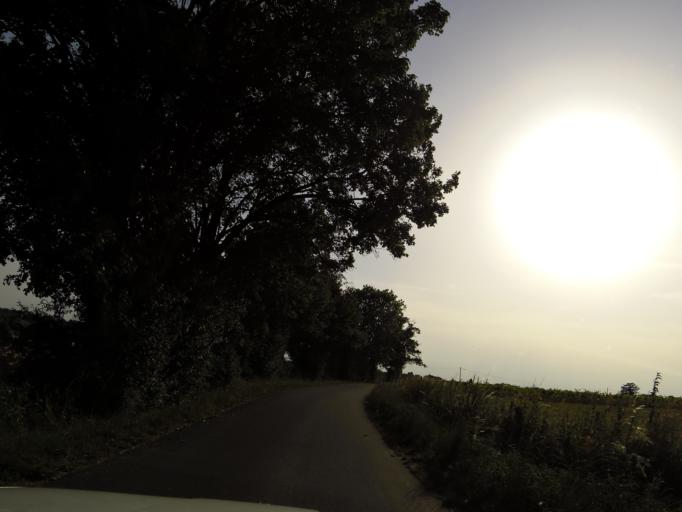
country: FR
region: Rhone-Alpes
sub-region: Departement de l'Ain
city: Perouges
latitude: 45.9334
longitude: 5.1726
